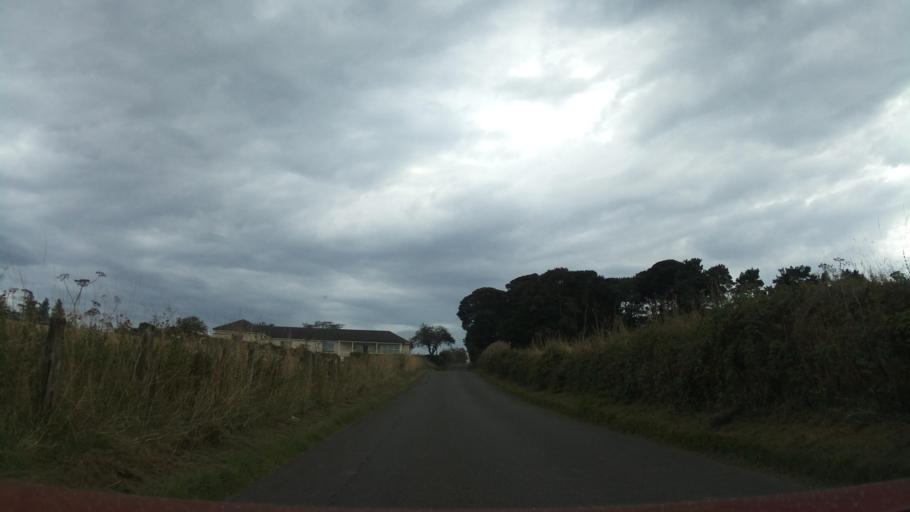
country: GB
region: Scotland
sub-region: Fife
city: Saint Andrews
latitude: 56.3201
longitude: -2.7800
